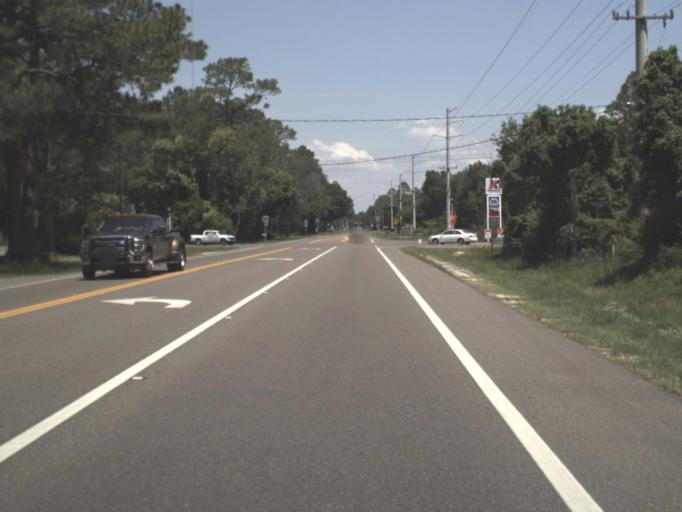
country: US
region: Florida
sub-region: Bradford County
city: Starke
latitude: 29.9265
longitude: -82.1003
